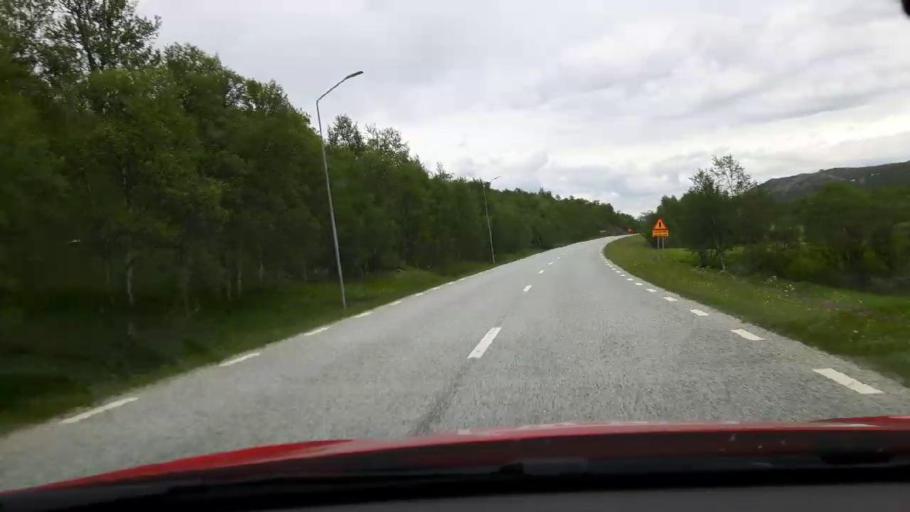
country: NO
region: Sor-Trondelag
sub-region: Tydal
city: Aas
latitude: 62.5923
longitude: 12.1887
